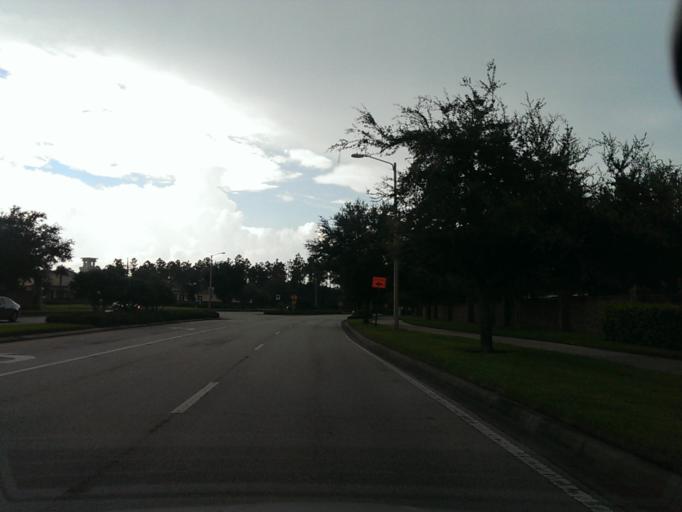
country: US
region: Florida
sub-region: Orange County
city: Winter Garden
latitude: 28.5345
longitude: -81.5823
